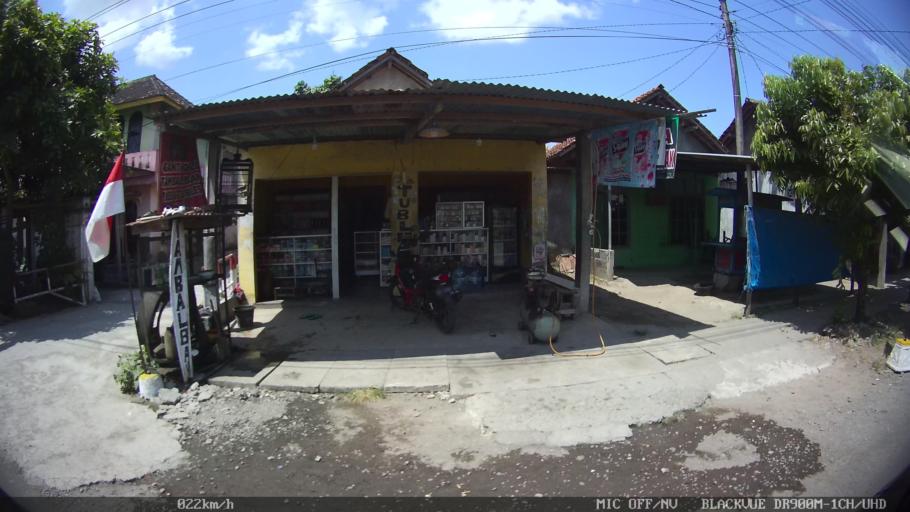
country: ID
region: Daerah Istimewa Yogyakarta
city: Sewon
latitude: -7.8993
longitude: 110.3843
